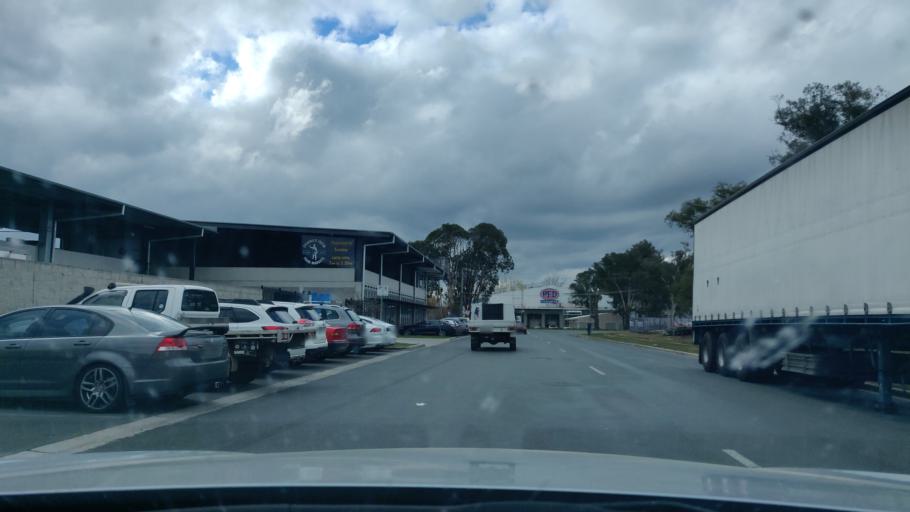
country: AU
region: Australian Capital Territory
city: Forrest
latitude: -35.3246
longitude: 149.1559
